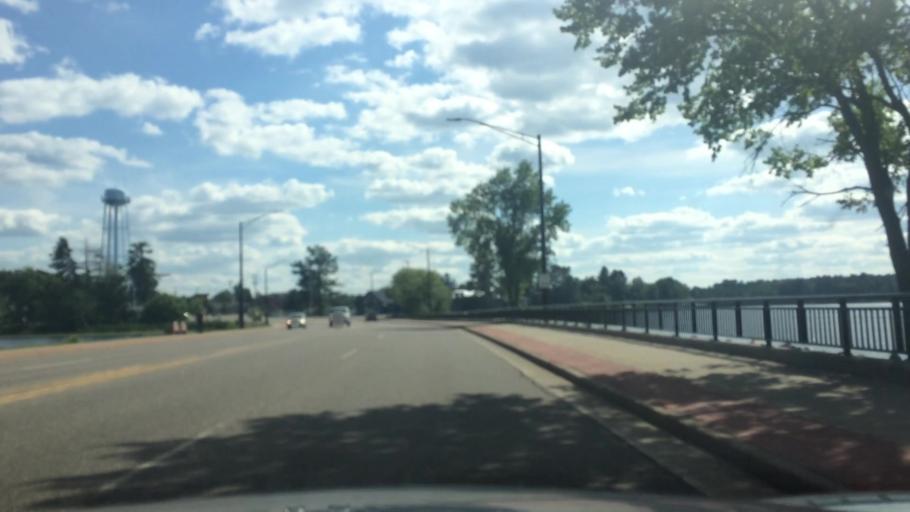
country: US
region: Wisconsin
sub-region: Vilas County
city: Lac du Flambeau
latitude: 45.8761
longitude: -89.7054
